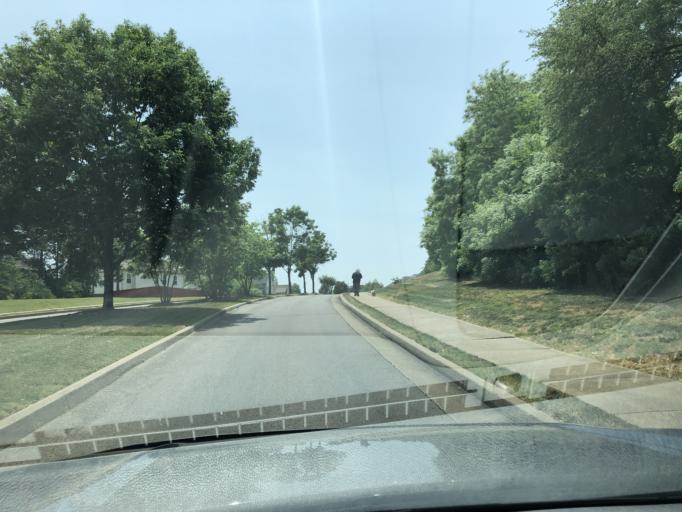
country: US
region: Tennessee
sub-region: Rutherford County
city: La Vergne
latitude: 36.0475
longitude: -86.6177
